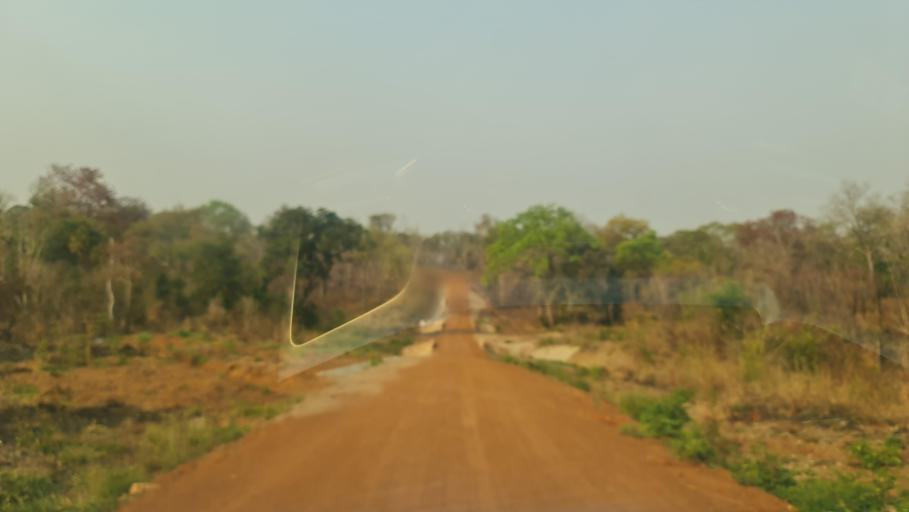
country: MZ
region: Zambezia
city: Quelimane
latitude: -17.1407
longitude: 37.1362
